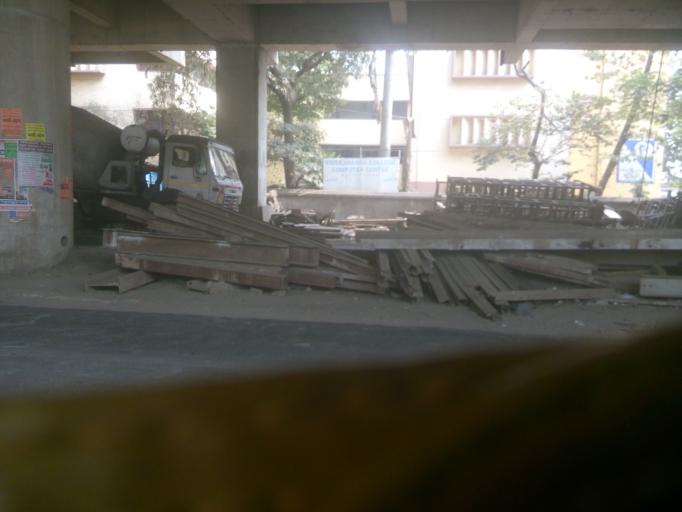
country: IN
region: West Bengal
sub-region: South 24 Paraganas
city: Santoshpur
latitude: 22.4644
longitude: 88.3075
